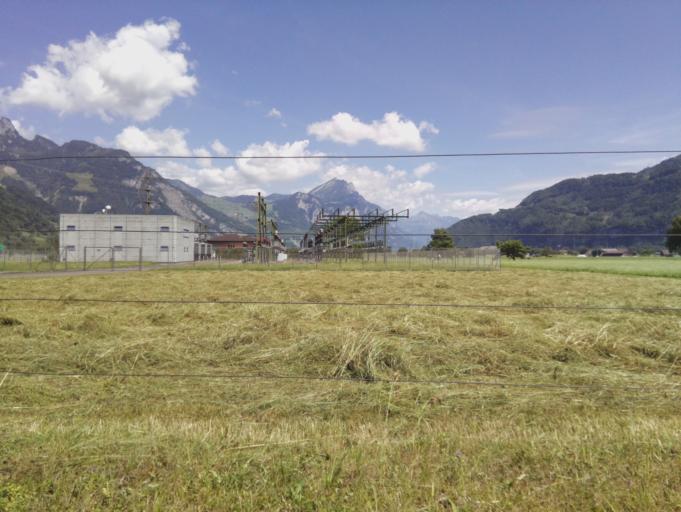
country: CH
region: Glarus
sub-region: Glarus
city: Niederurnen
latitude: 47.1247
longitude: 9.0652
